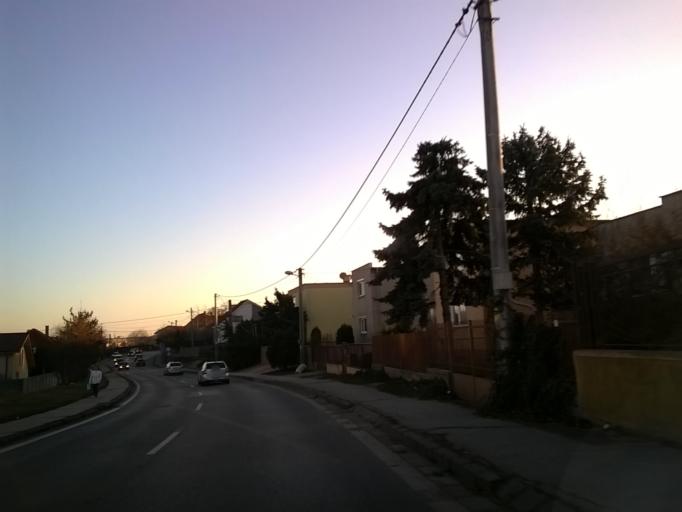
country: SK
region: Nitriansky
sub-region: Okres Nitra
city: Nitra
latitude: 48.2956
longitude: 18.0697
